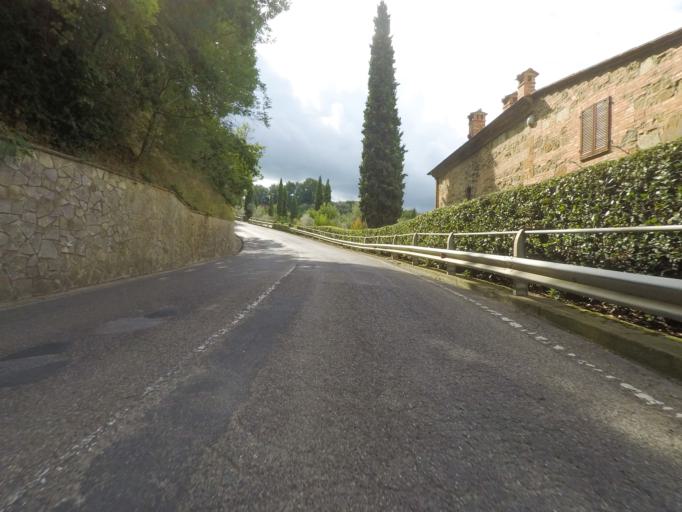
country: IT
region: Tuscany
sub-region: Provincia di Siena
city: Montepulciano
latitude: 43.1121
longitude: 11.7887
